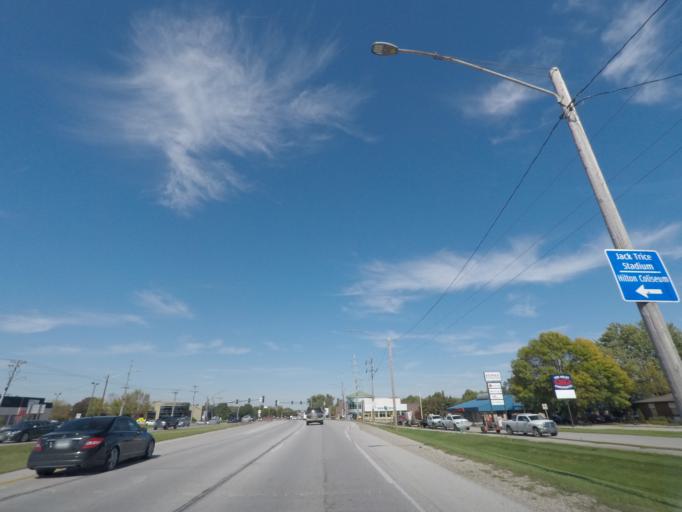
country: US
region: Iowa
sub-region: Story County
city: Ames
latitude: 42.0072
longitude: -93.6099
